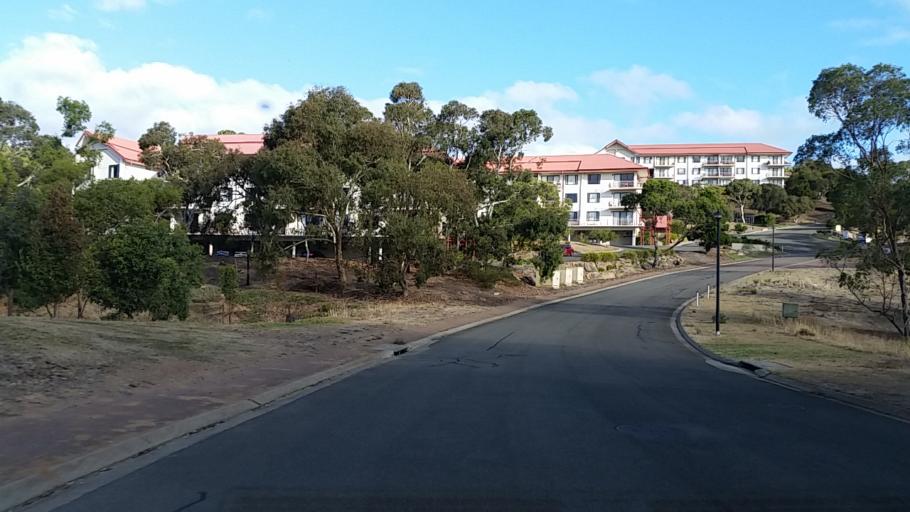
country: AU
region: South Australia
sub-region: Yankalilla
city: Normanville
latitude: -35.5060
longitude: 138.2460
